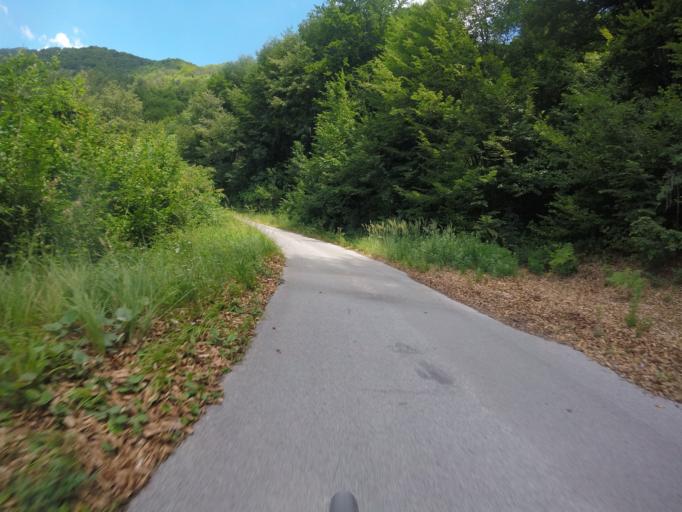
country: SI
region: Kostanjevica na Krki
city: Kostanjevica na Krki
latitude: 45.7712
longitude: 15.4165
